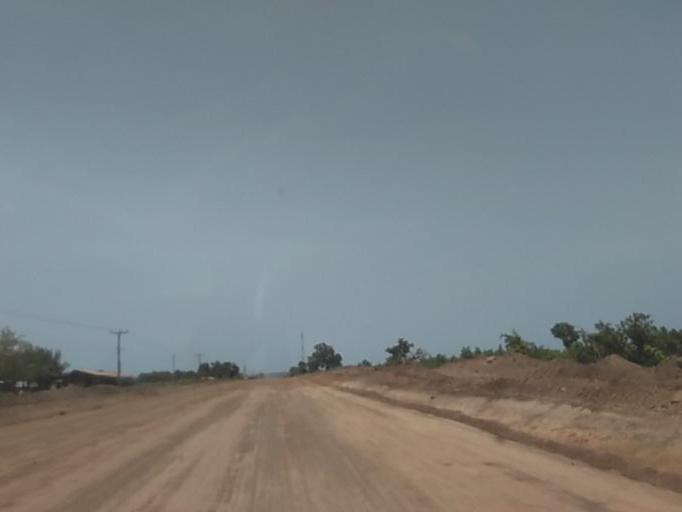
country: GH
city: Kpandae
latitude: 8.6379
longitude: 0.2224
